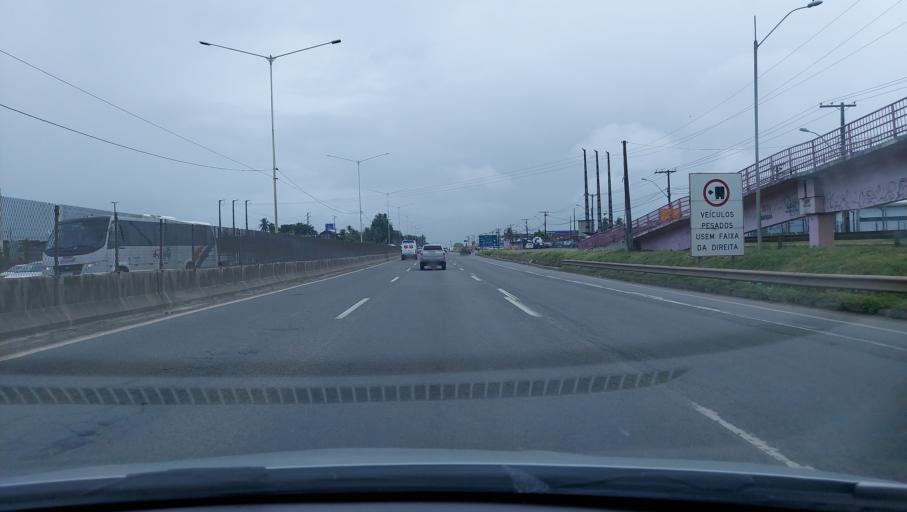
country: BR
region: Bahia
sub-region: Salvador
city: Salvador
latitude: -12.8967
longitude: -38.4490
